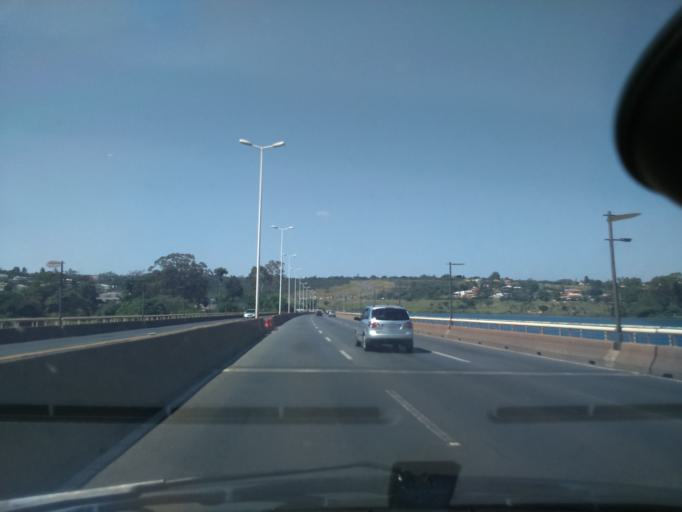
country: BR
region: Federal District
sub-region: Brasilia
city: Brasilia
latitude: -15.8266
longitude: -47.8279
